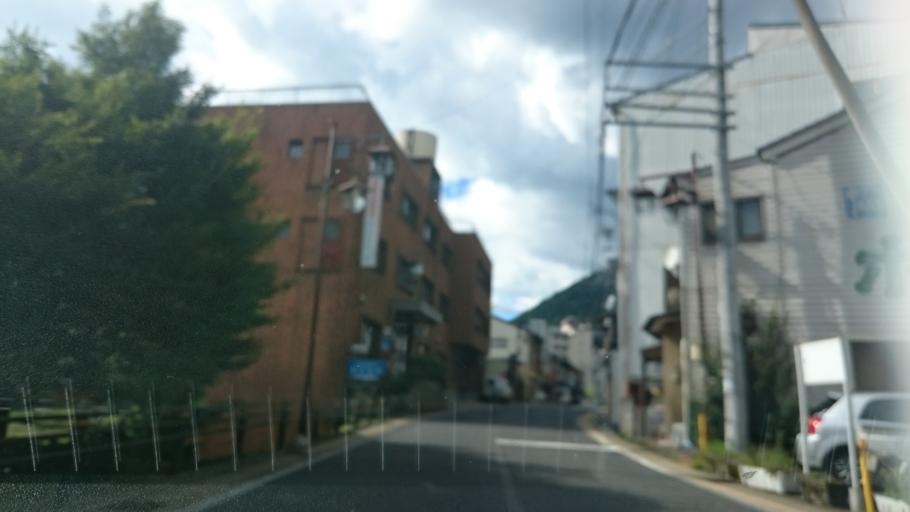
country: JP
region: Gifu
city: Gujo
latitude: 35.8058
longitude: 137.2433
